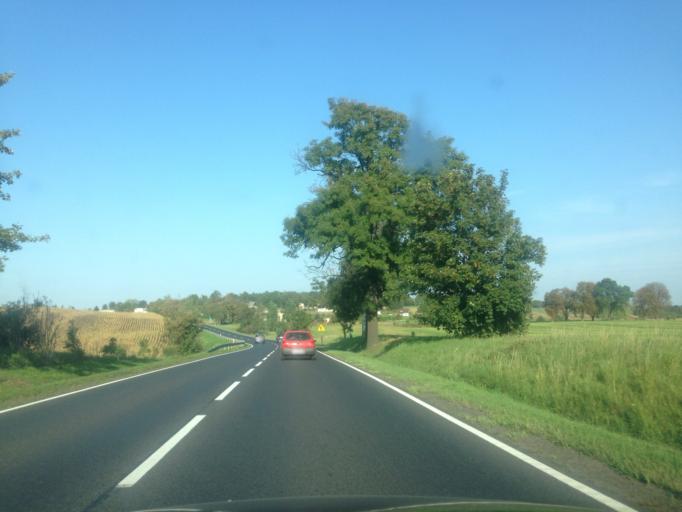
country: PL
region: Kujawsko-Pomorskie
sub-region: Powiat brodnicki
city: Brodnica
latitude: 53.2916
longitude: 19.4969
